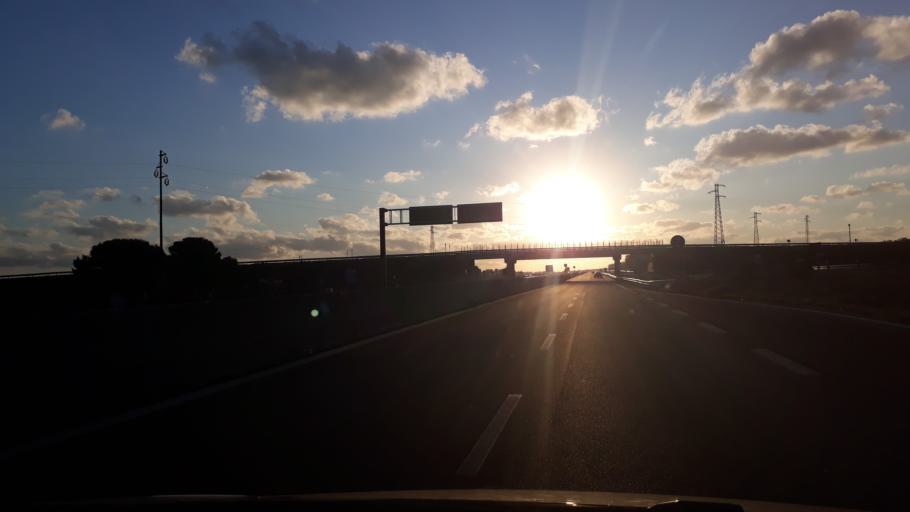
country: IT
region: Apulia
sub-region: Provincia di Brindisi
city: San Vito dei Normanni
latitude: 40.7286
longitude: 17.7376
